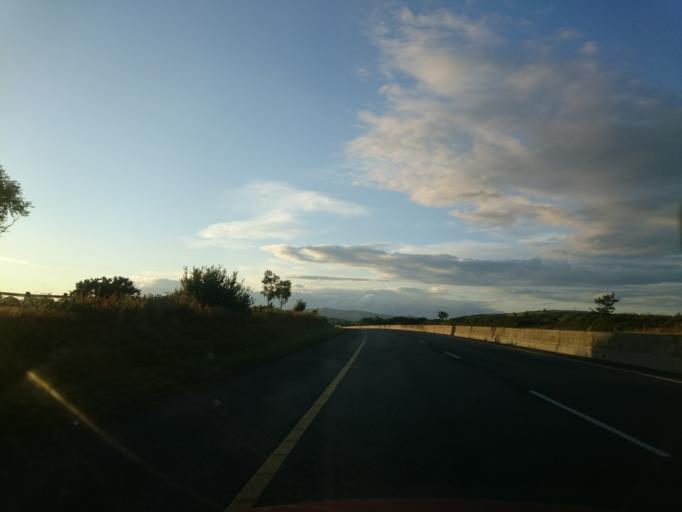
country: IE
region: Leinster
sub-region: Loch Garman
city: Gorey
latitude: 52.6777
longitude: -6.2581
